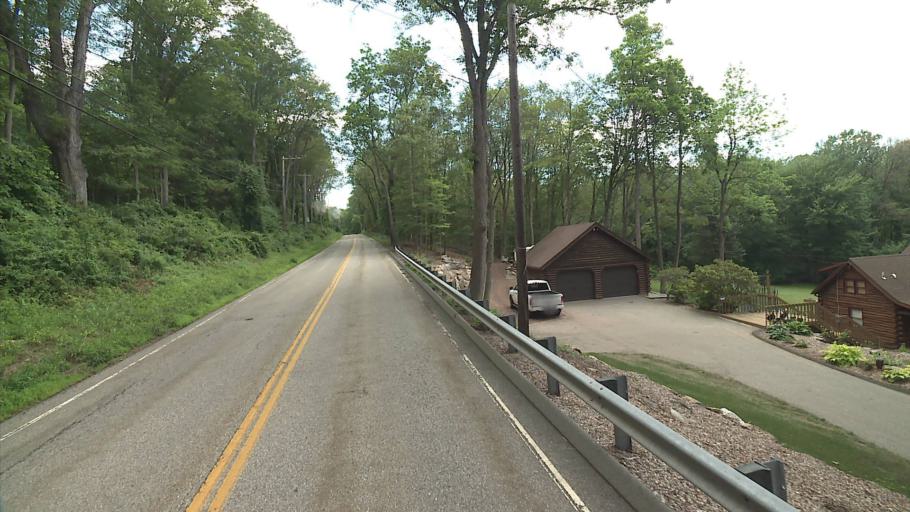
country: US
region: Connecticut
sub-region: Middlesex County
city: Higganum
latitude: 41.5334
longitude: -72.5413
